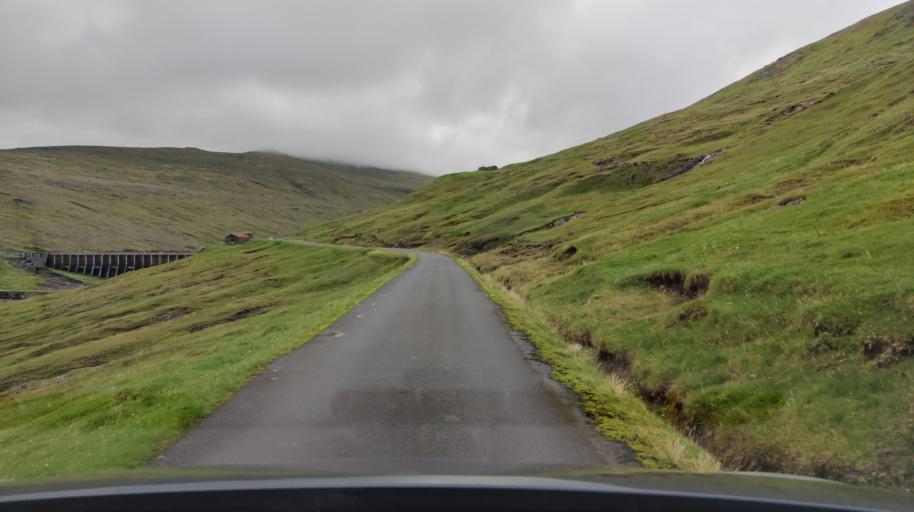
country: FO
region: Streymoy
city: Vestmanna
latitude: 62.1743
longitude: -7.1489
